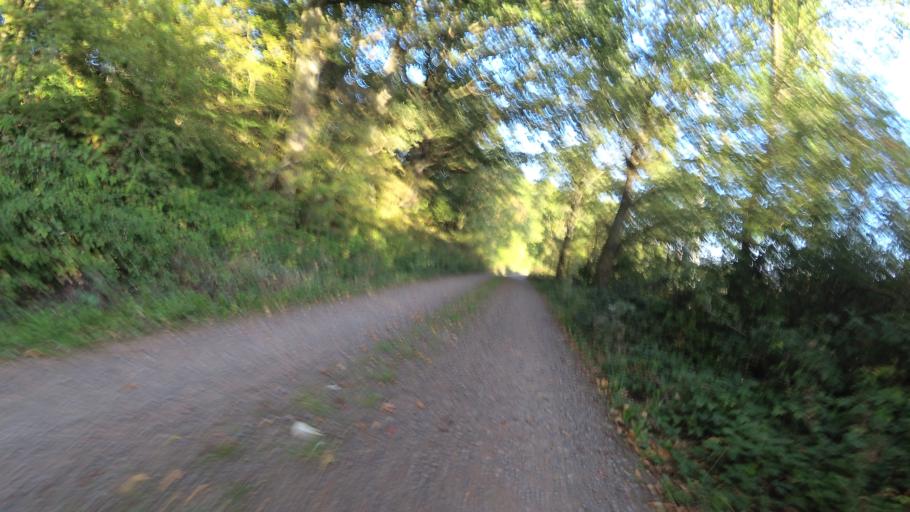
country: DE
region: Rheinland-Pfalz
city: Breitenbach
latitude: 49.4386
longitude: 7.2145
